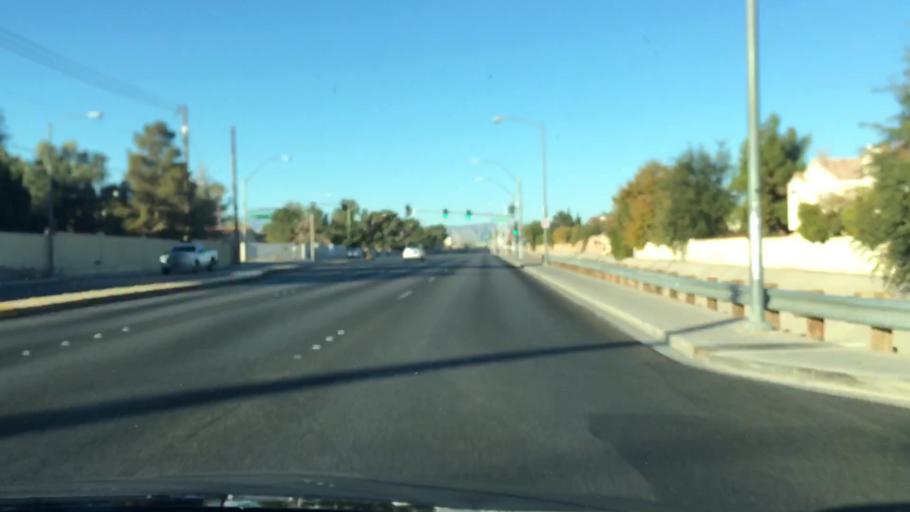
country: US
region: Nevada
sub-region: Clark County
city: Paradise
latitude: 36.0426
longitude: -115.1442
